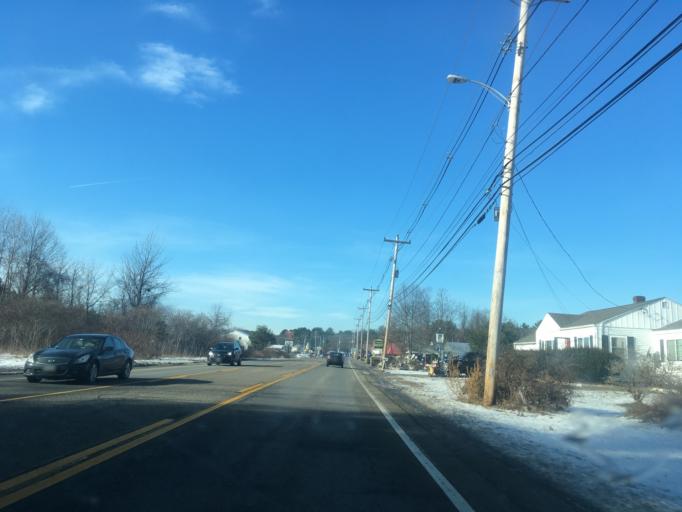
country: US
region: Massachusetts
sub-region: Essex County
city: Salisbury
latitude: 42.8425
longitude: -70.8742
